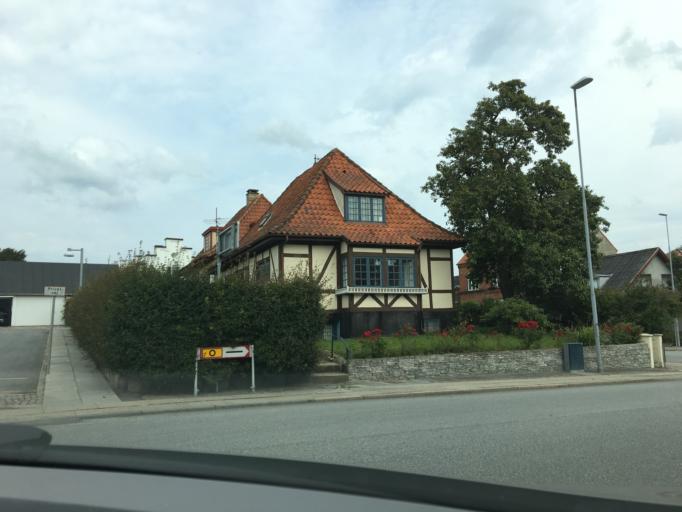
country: DK
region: Central Jutland
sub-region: Skive Kommune
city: Skive
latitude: 56.5701
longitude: 9.0281
